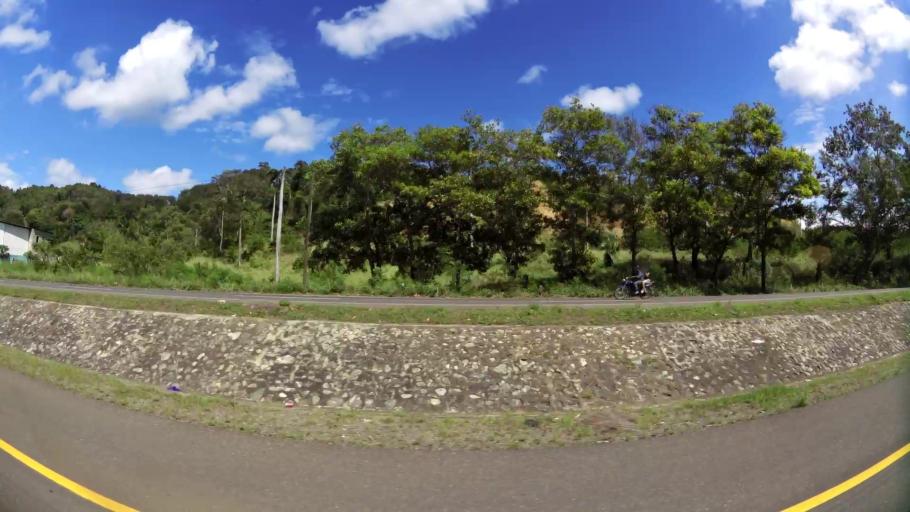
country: DO
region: La Vega
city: Rio Verde Arriba
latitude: 19.2764
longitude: -70.5699
